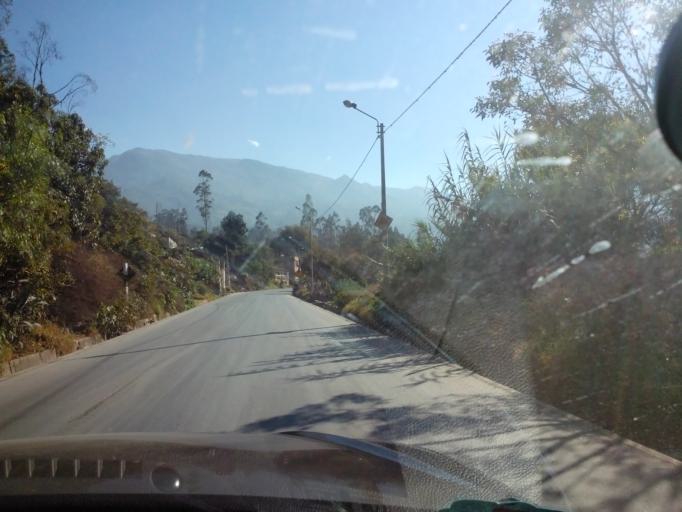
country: PE
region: Apurimac
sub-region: Provincia de Abancay
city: Tamburco
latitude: -13.6225
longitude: -72.8717
